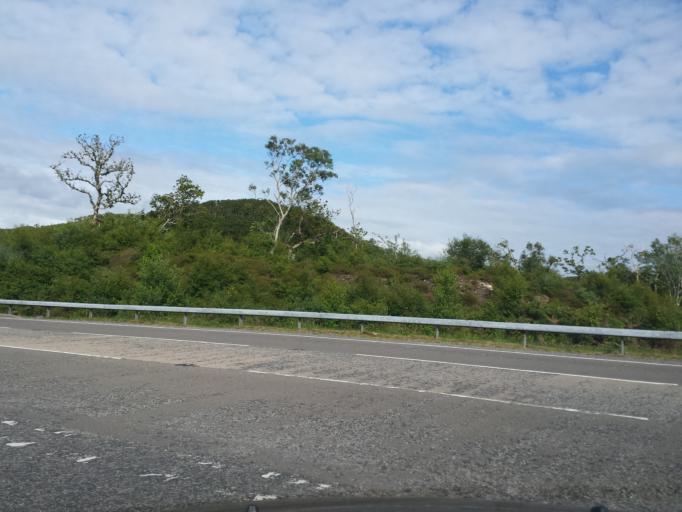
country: GB
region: Scotland
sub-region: Argyll and Bute
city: Isle Of Mull
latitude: 56.9592
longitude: -5.8195
